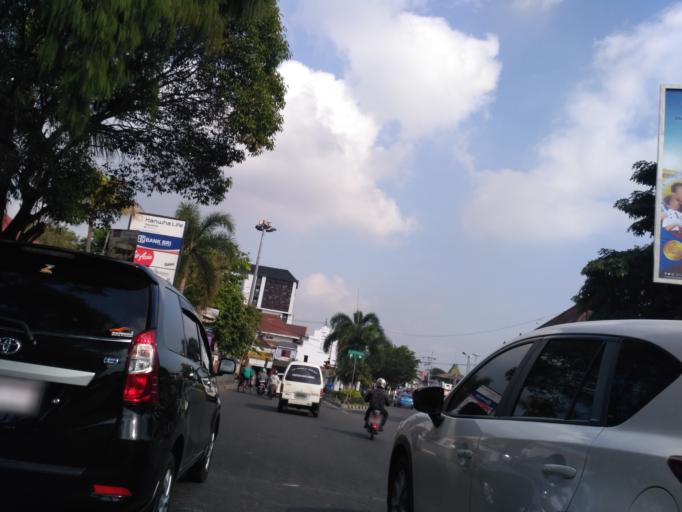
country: ID
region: Daerah Istimewa Yogyakarta
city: Yogyakarta
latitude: -7.7901
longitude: 110.3670
